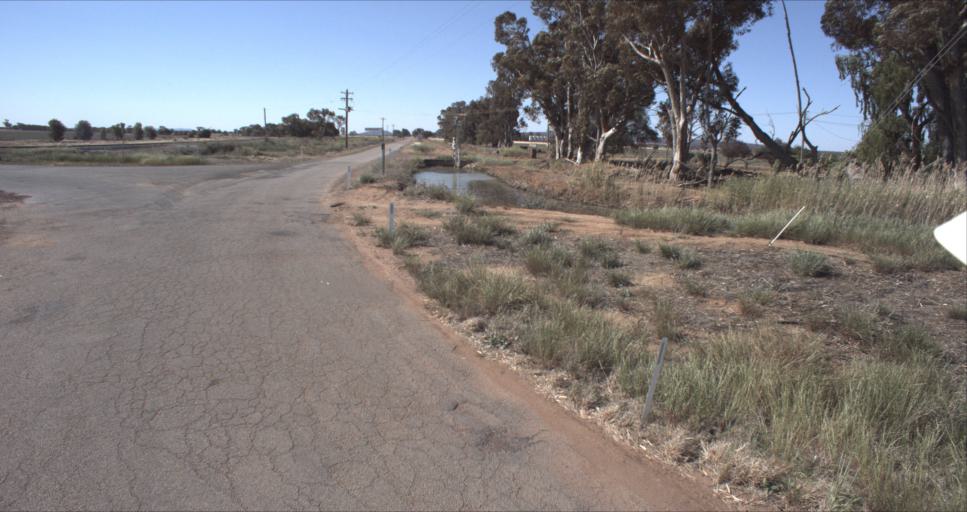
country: AU
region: New South Wales
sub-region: Leeton
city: Leeton
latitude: -34.4782
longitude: 146.3680
